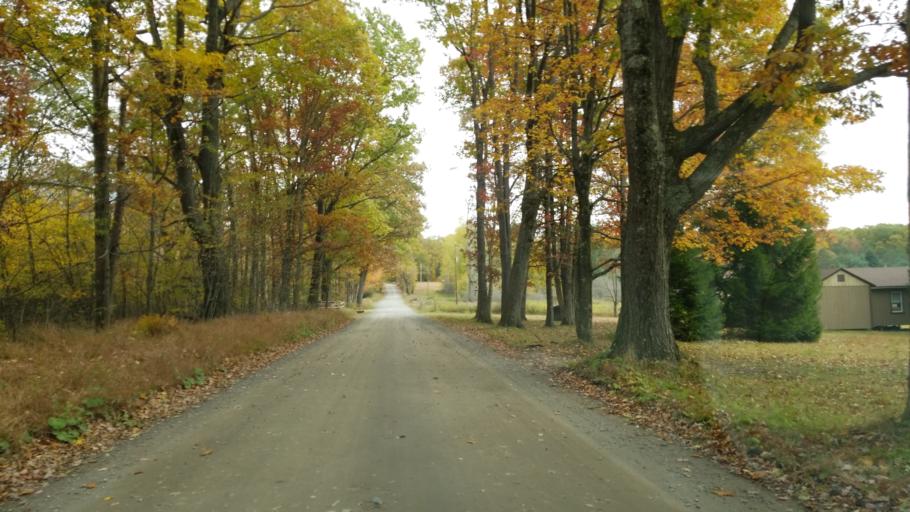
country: US
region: Pennsylvania
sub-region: Clearfield County
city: Shiloh
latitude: 41.1874
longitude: -78.3634
